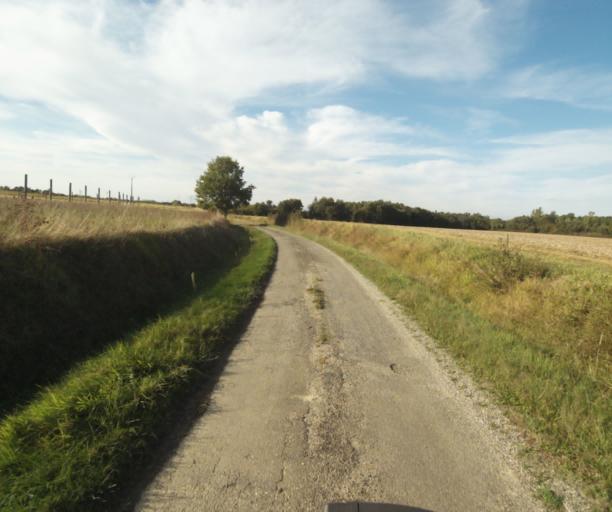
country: FR
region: Midi-Pyrenees
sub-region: Departement du Tarn-et-Garonne
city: Finhan
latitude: 43.9093
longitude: 1.1110
